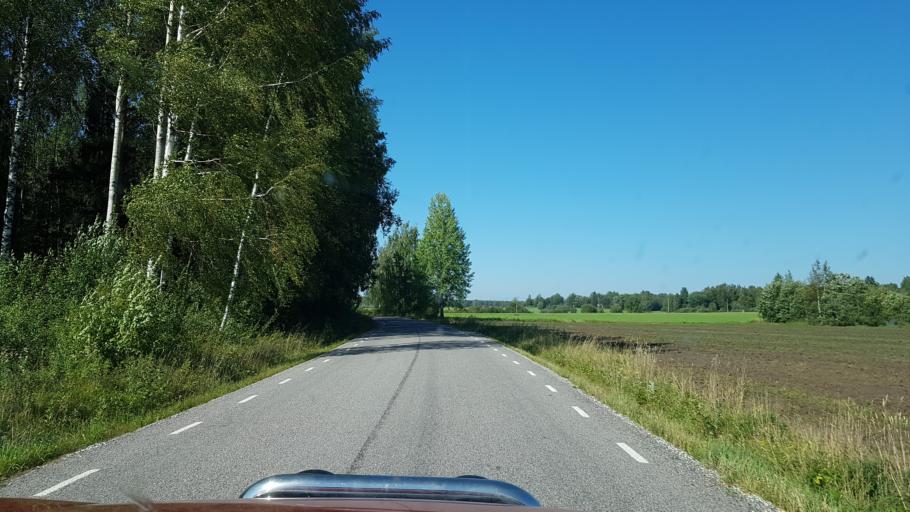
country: EE
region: Polvamaa
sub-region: Polva linn
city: Polva
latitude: 58.2170
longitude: 27.2141
